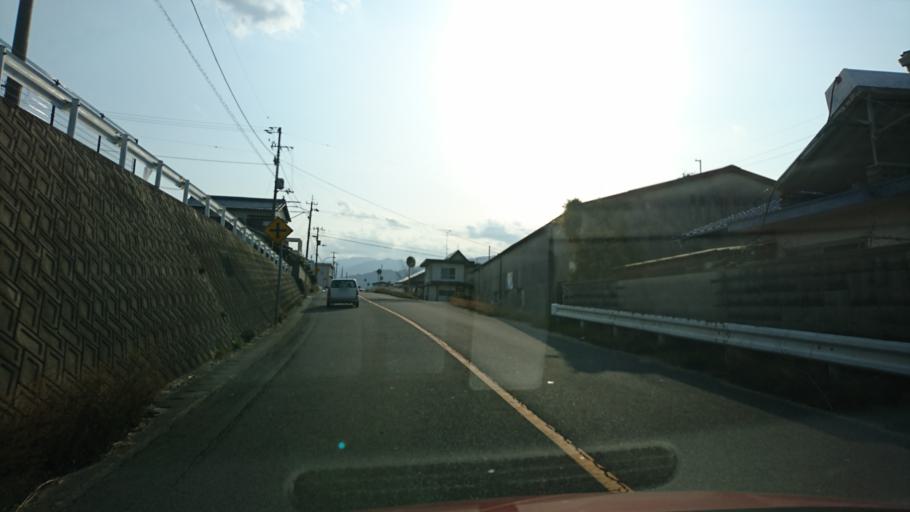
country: JP
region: Ehime
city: Saijo
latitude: 34.0289
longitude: 133.0147
